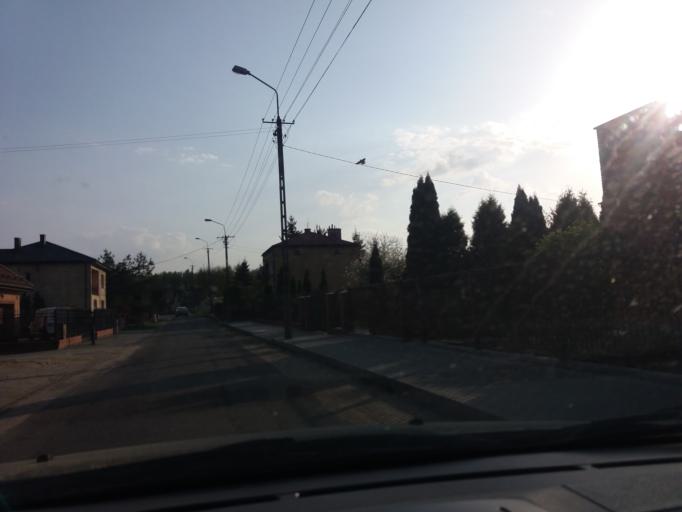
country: PL
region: Masovian Voivodeship
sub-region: Powiat mlawski
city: Mlawa
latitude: 53.1265
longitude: 20.3443
